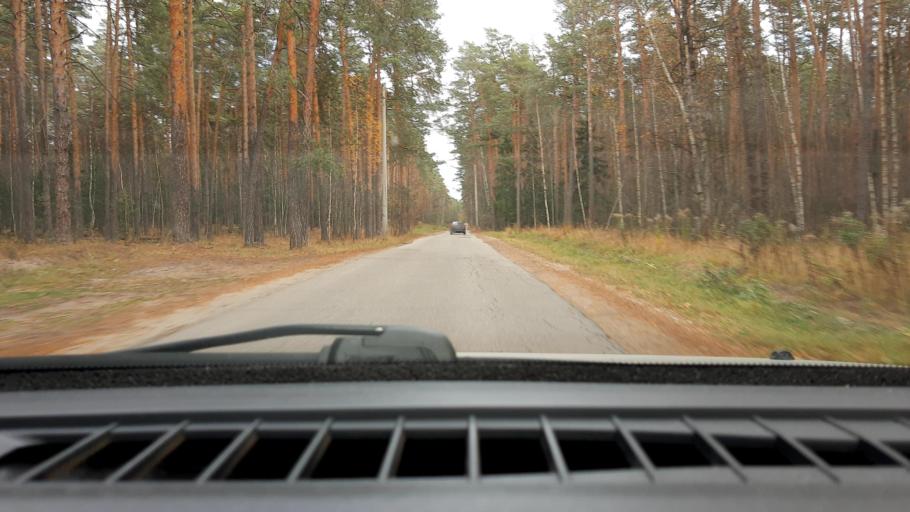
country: RU
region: Nizjnij Novgorod
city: Kstovo
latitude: 56.1684
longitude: 44.1079
